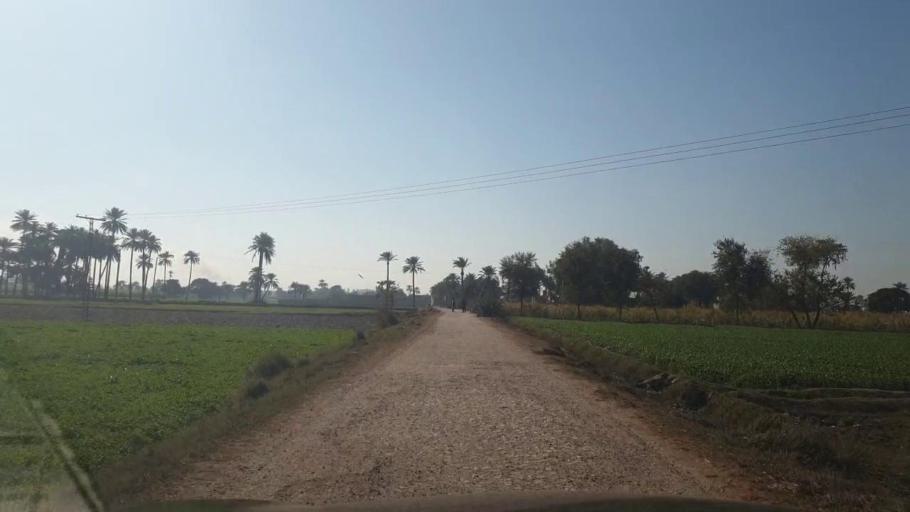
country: PK
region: Sindh
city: Ghotki
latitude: 27.9978
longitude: 69.3273
